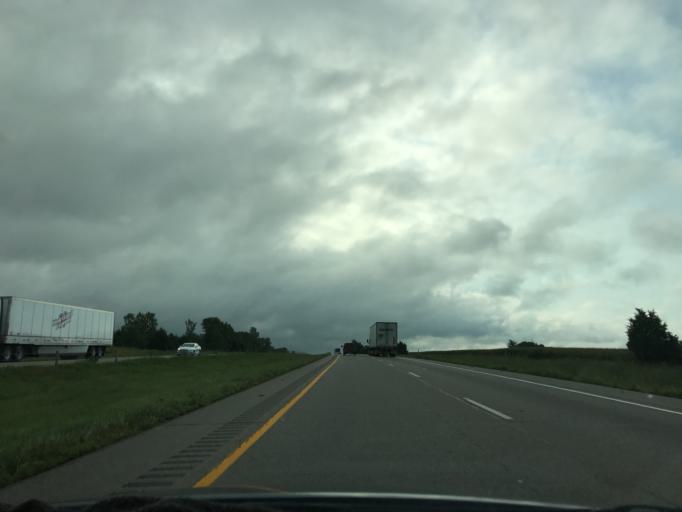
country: US
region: Iowa
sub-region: Muscatine County
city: West Liberty
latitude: 41.6520
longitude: -91.1825
